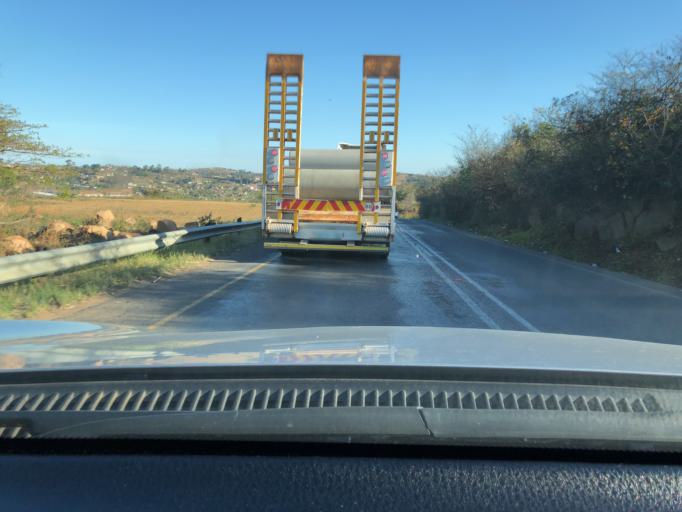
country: ZA
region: KwaZulu-Natal
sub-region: eThekwini Metropolitan Municipality
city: Umkomaas
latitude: -30.0308
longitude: 30.8111
